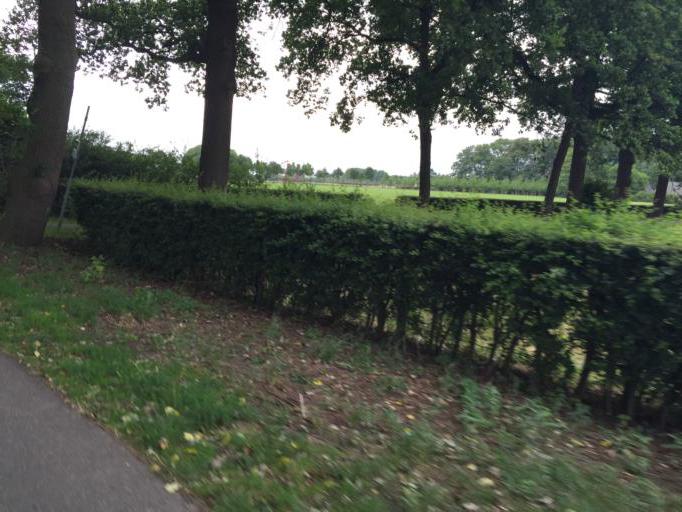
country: NL
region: Utrecht
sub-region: Gemeente Bunnik
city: Bunnik
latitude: 52.0742
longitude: 5.1839
